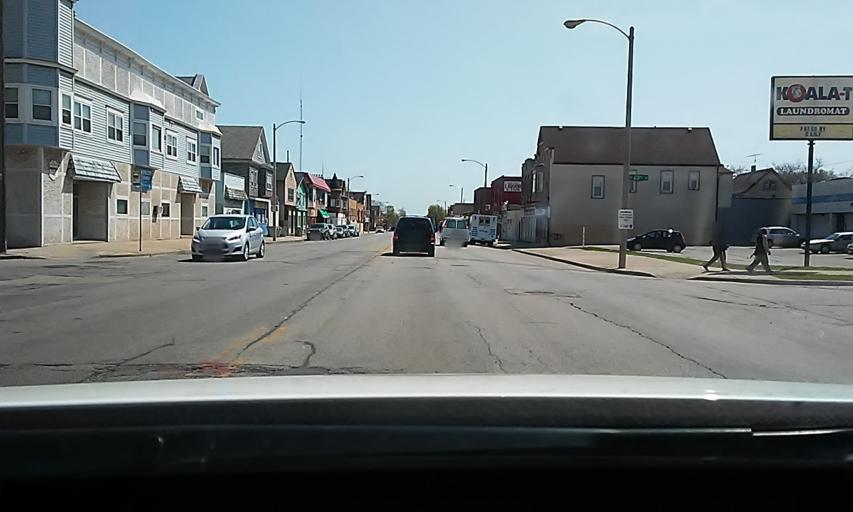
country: US
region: Wisconsin
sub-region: Milwaukee County
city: West Milwaukee
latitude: 43.0225
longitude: -87.9425
